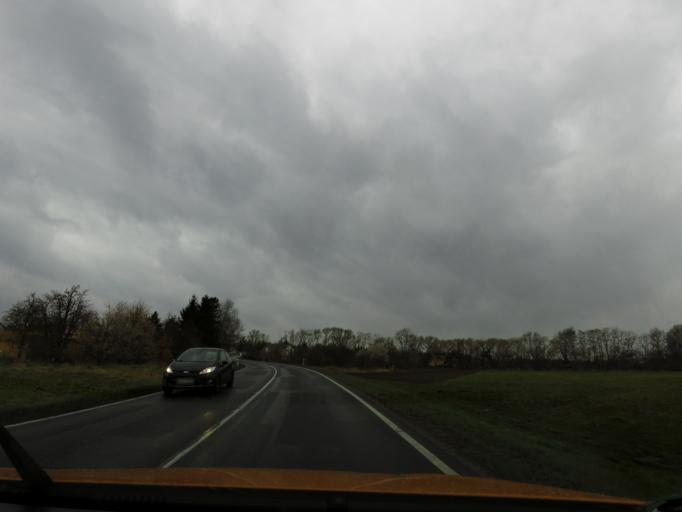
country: DE
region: Brandenburg
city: Ziesar
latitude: 52.2716
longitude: 12.2896
